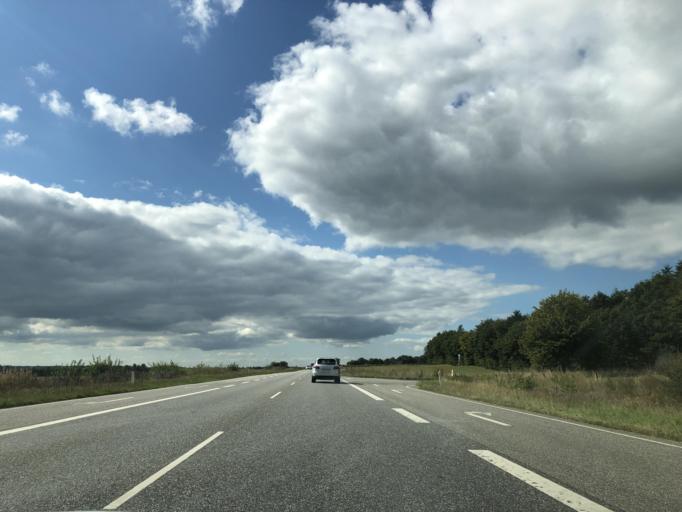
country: DK
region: North Denmark
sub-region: Vesthimmerland Kommune
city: Aars
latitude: 56.7864
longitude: 9.5979
